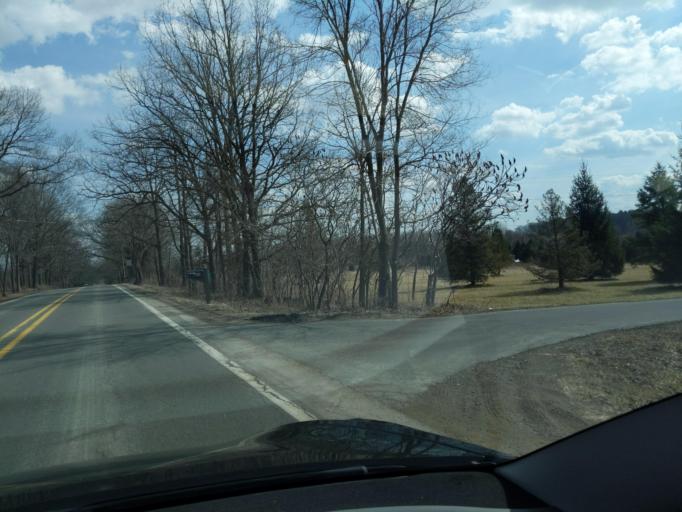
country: US
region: Michigan
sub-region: Washtenaw County
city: Dexter
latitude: 42.3841
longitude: -83.8922
